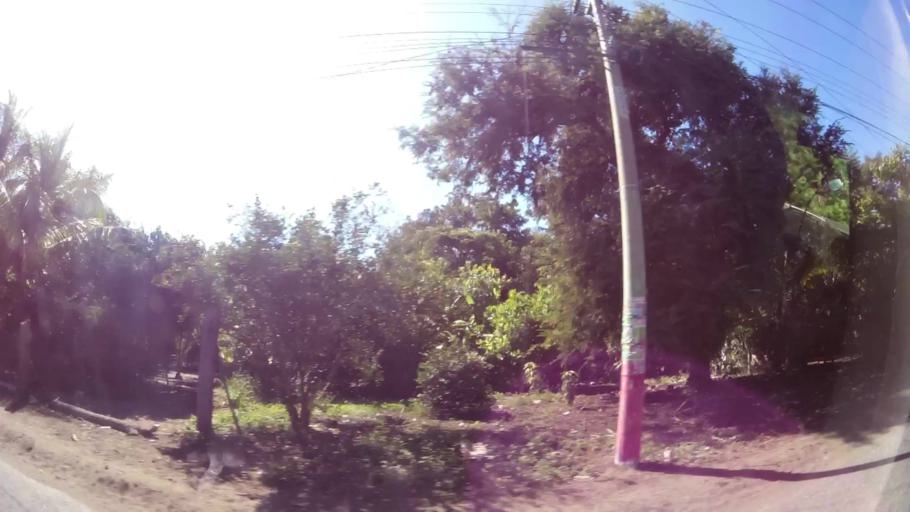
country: GT
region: Escuintla
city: Iztapa
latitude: 13.9213
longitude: -90.5679
